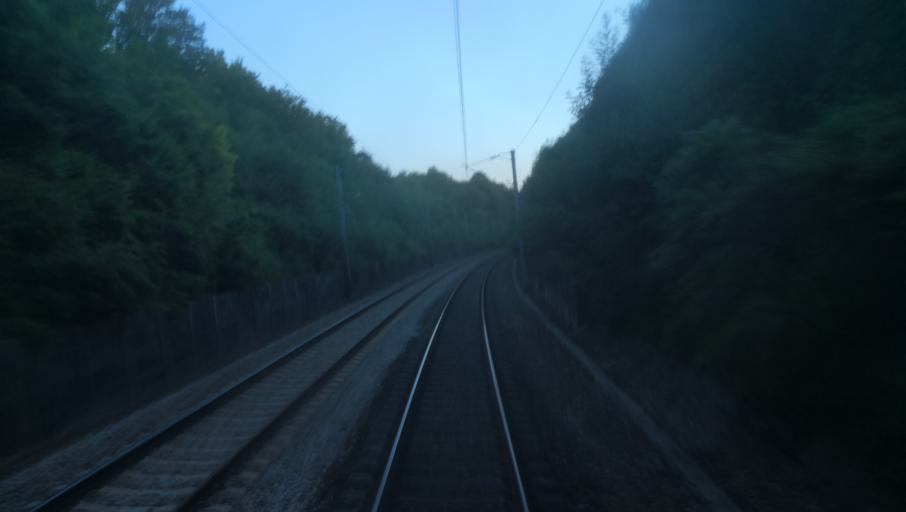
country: FR
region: Ile-de-France
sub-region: Departement des Yvelines
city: Breval
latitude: 48.9167
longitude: 1.5149
